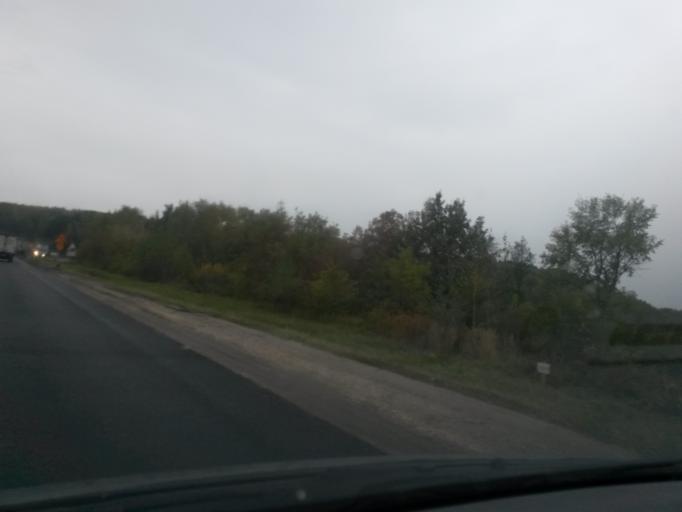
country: RU
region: Nizjnij Novgorod
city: Pamyat' Parizhskoy Kommuny
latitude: 56.0723
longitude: 44.3725
